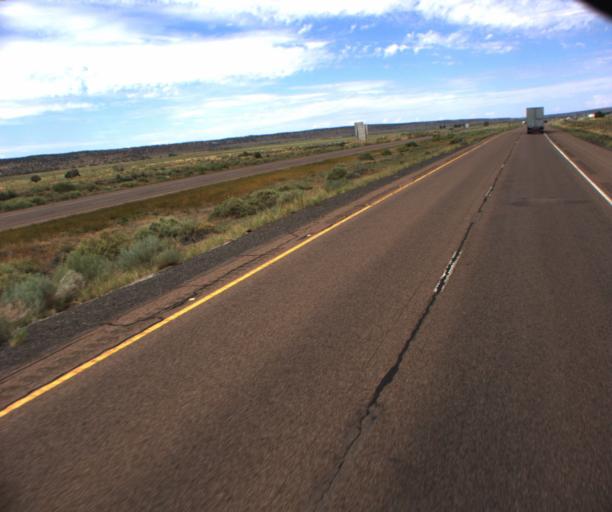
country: US
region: Arizona
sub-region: Apache County
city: Houck
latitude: 35.2090
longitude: -109.3502
